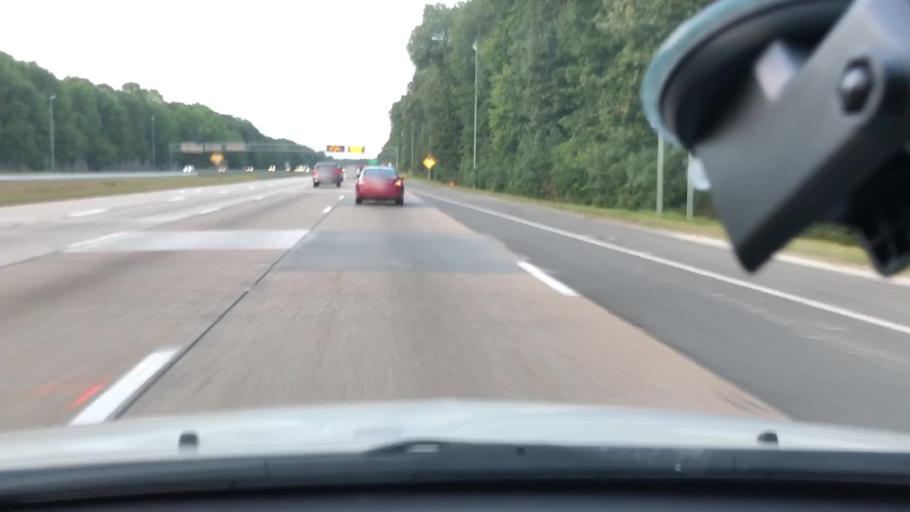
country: US
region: Virginia
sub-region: City of Chesapeake
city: Chesapeake
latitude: 36.7918
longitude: -76.2148
